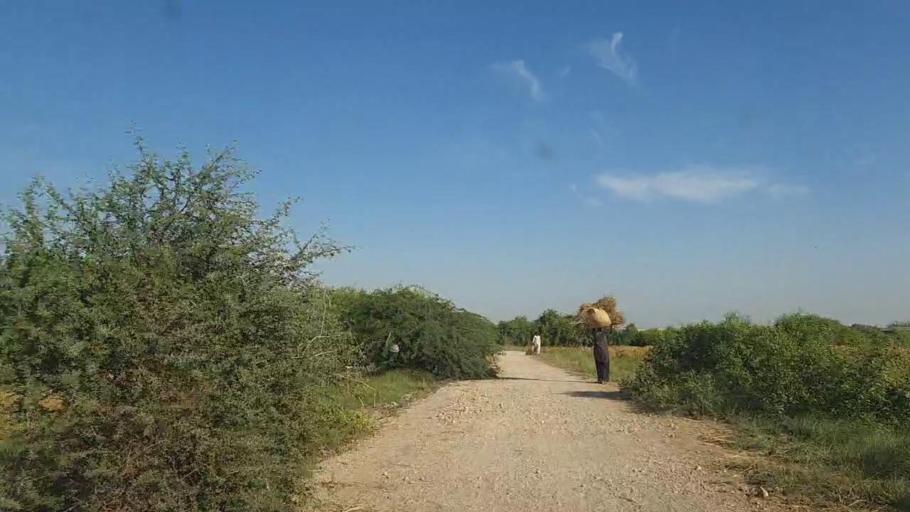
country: PK
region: Sindh
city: Mirpur Batoro
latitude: 24.7619
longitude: 68.3560
